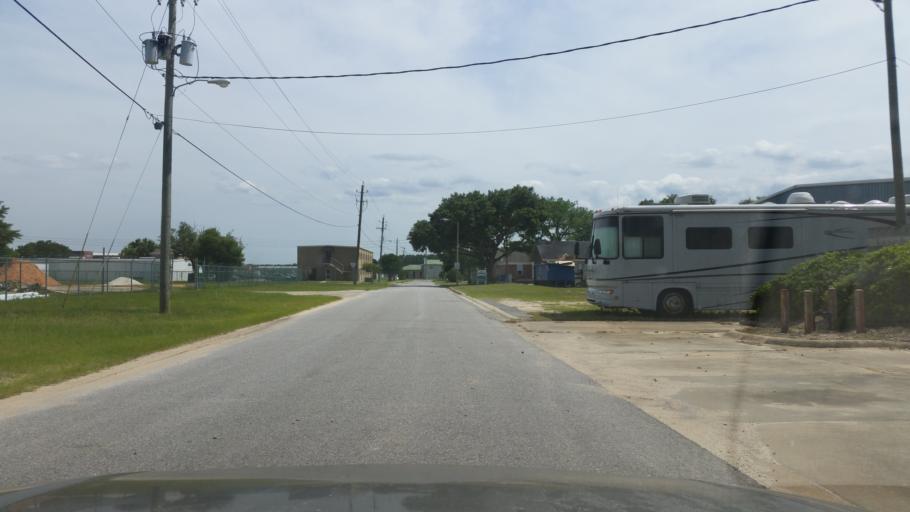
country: US
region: Florida
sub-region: Escambia County
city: Ferry Pass
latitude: 30.5304
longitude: -87.2019
